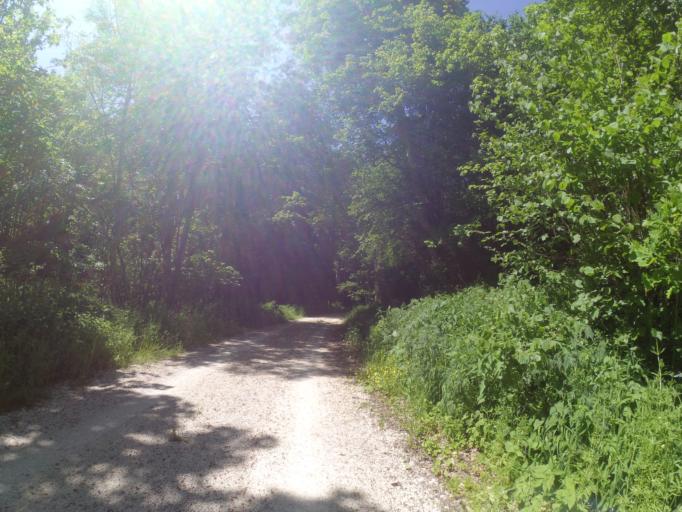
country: DE
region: Baden-Wuerttemberg
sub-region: Tuebingen Region
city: Berghulen
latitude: 48.4802
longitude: 9.8059
